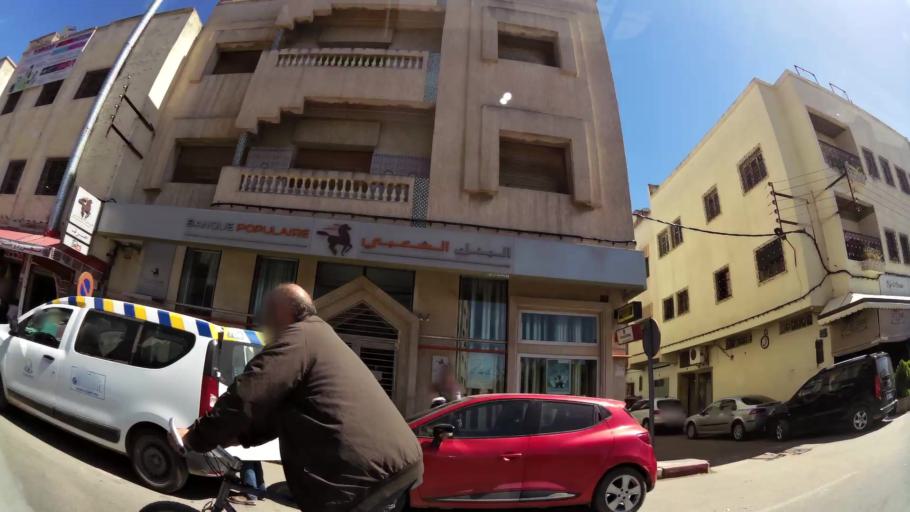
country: MA
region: Fes-Boulemane
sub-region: Fes
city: Fes
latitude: 34.0174
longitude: -4.9887
